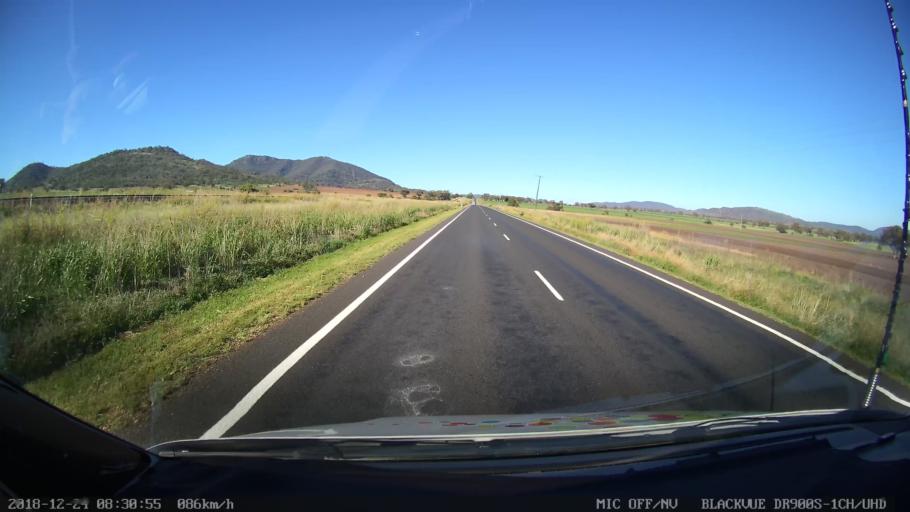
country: AU
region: New South Wales
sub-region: Tamworth Municipality
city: Phillip
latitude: -31.2702
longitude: 150.7186
